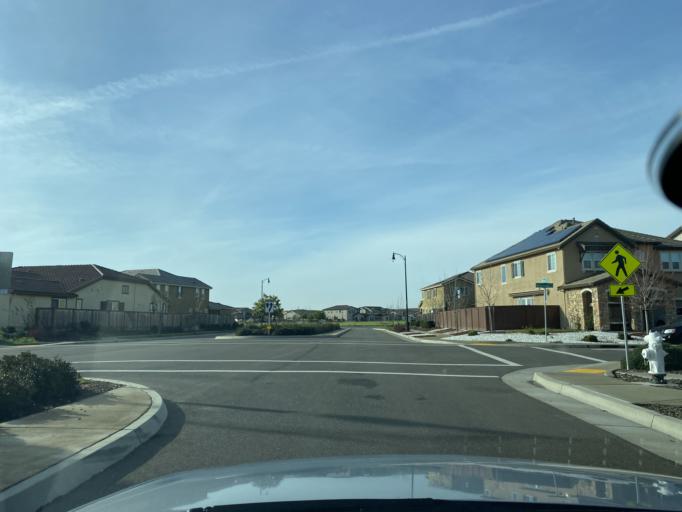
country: US
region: California
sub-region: Sacramento County
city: Elk Grove
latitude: 38.3992
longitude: -121.3882
